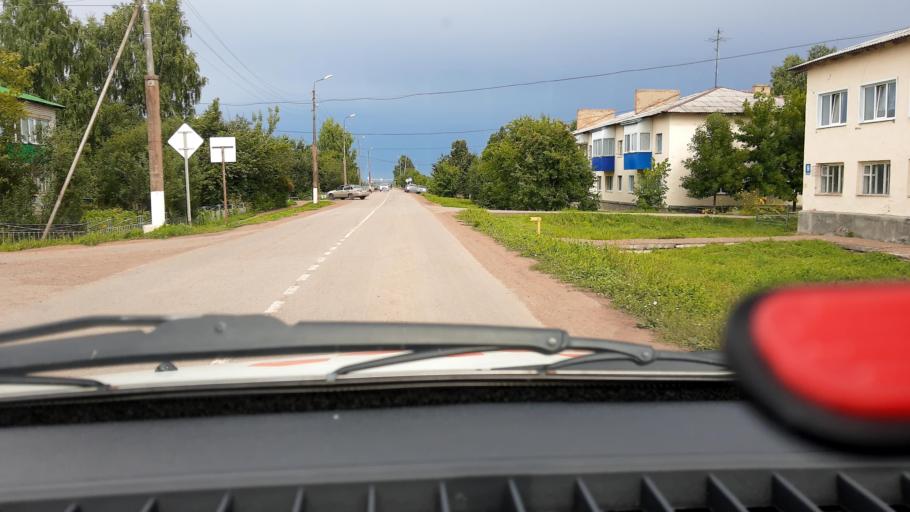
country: RU
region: Bashkortostan
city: Semiletka
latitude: 55.3631
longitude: 54.6114
